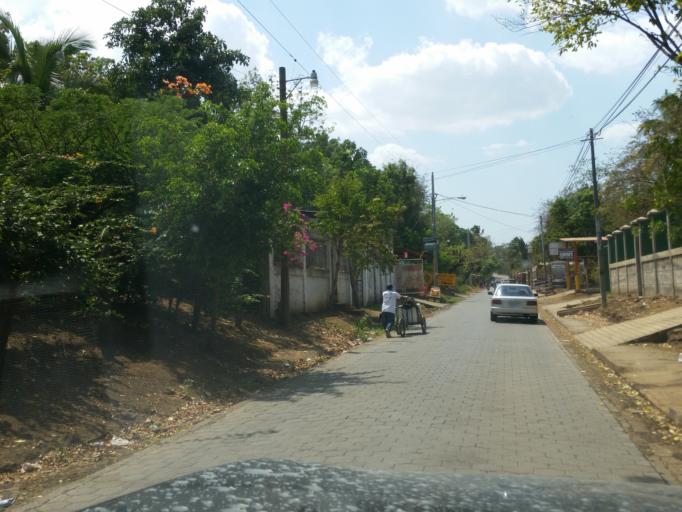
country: NI
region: Masaya
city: Ticuantepe
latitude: 12.0688
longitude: -86.2020
